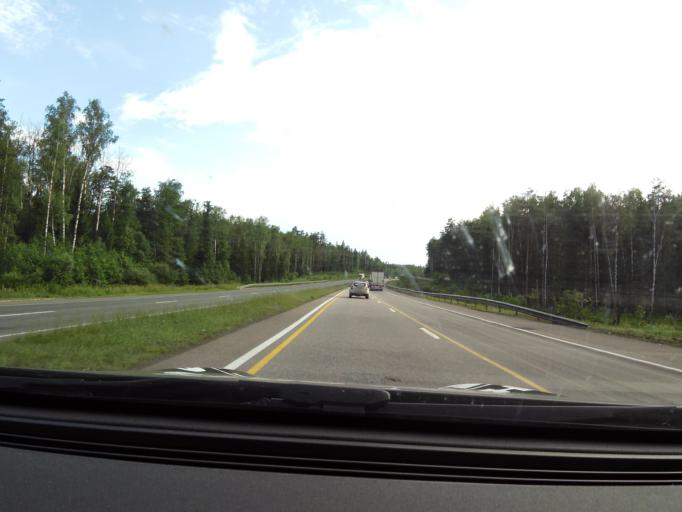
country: RU
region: Vladimir
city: Sudogda
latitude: 56.1504
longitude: 40.9171
